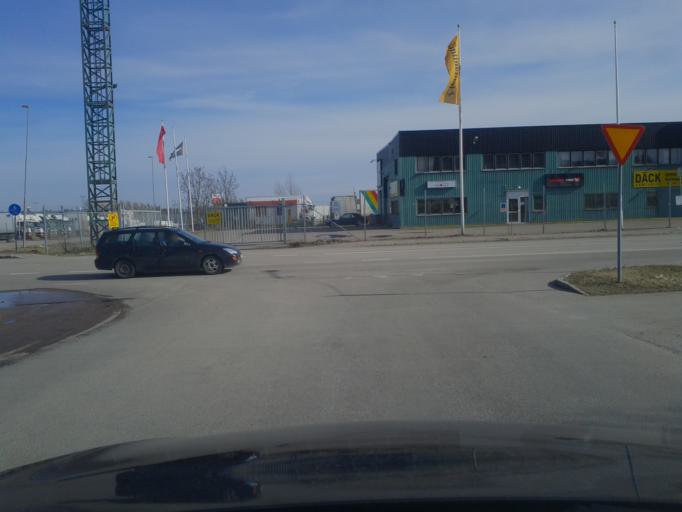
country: SE
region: Vaestmanland
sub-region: Vasteras
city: Vasteras
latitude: 59.6092
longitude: 16.6114
